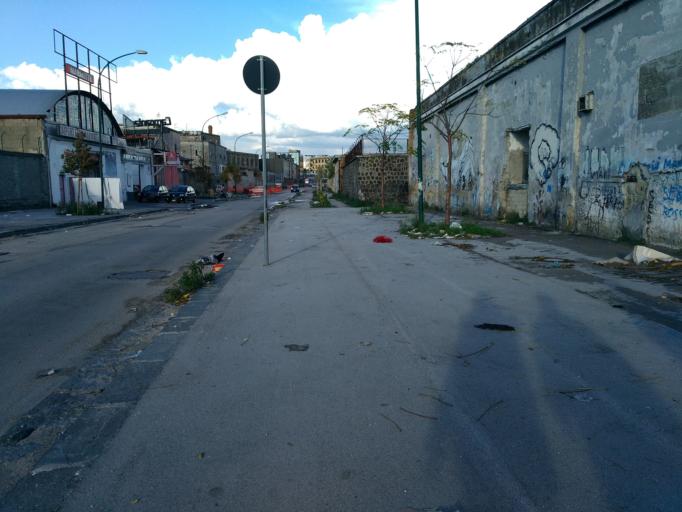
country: IT
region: Campania
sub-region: Provincia di Napoli
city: Napoli
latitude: 40.8458
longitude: 14.2892
